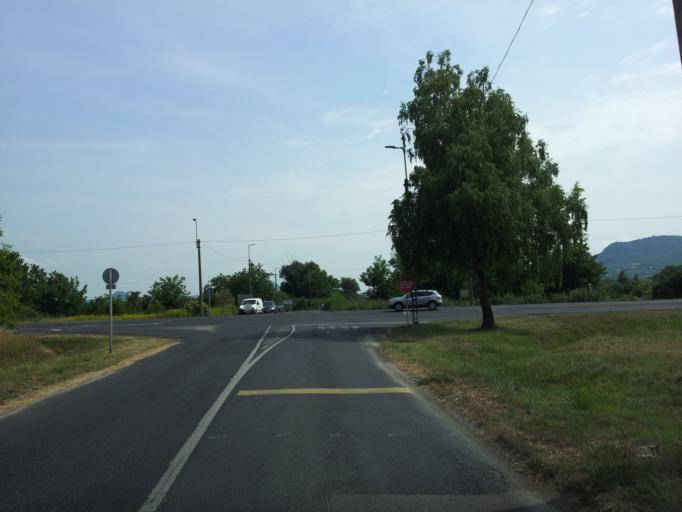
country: HU
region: Veszprem
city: Tapolca
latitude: 46.8773
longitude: 17.4447
